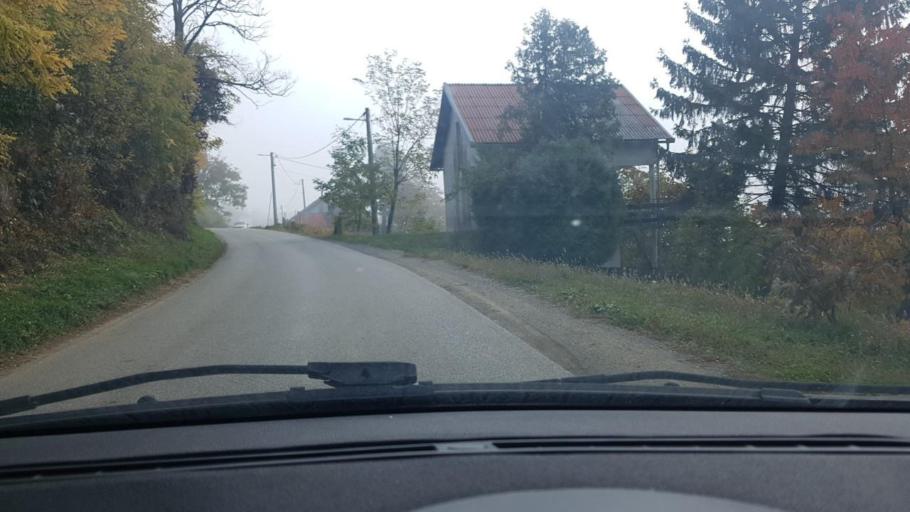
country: HR
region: Varazdinska
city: Lepoglava
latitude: 46.1563
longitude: 16.0276
